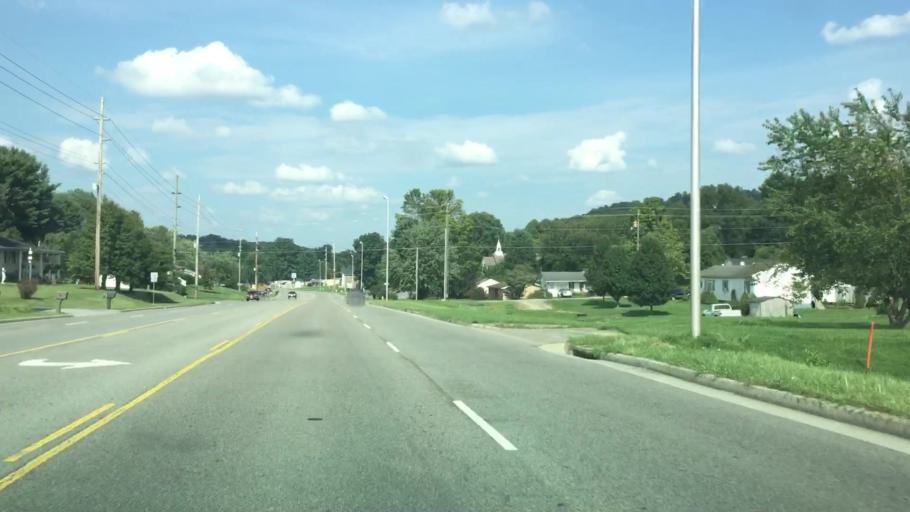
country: US
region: Tennessee
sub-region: Sullivan County
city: Fairmount
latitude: 36.6228
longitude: -82.1265
